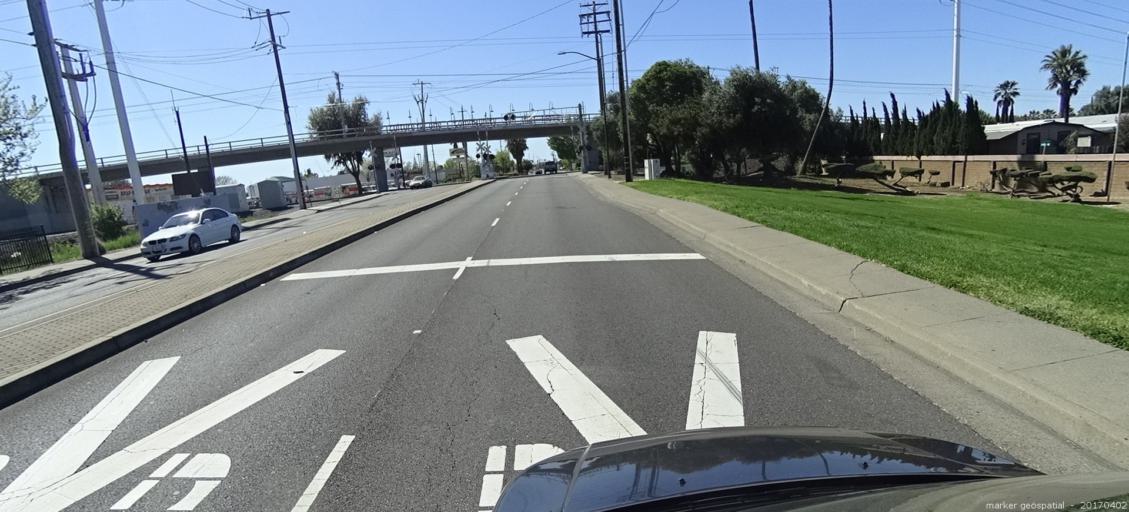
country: US
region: California
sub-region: Sacramento County
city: Parkway
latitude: 38.4960
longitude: -121.4700
